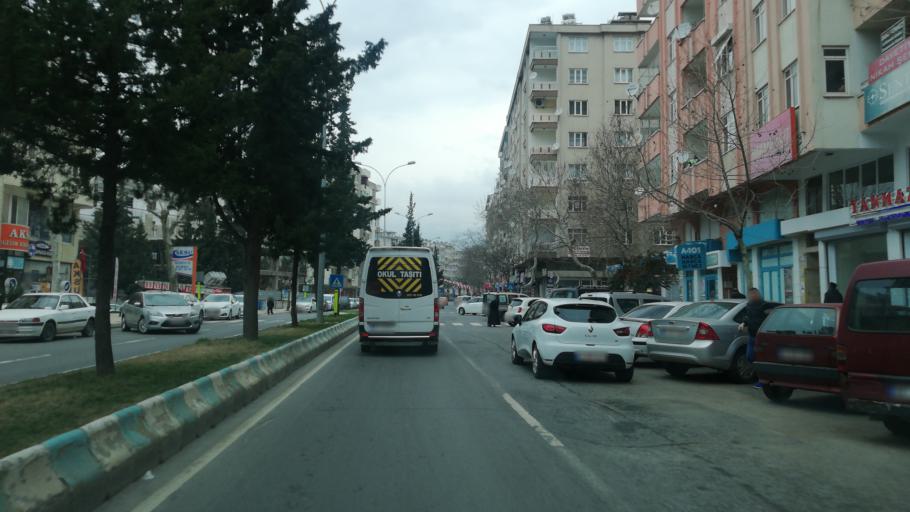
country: TR
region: Kahramanmaras
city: Kahramanmaras
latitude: 37.5736
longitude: 36.9350
